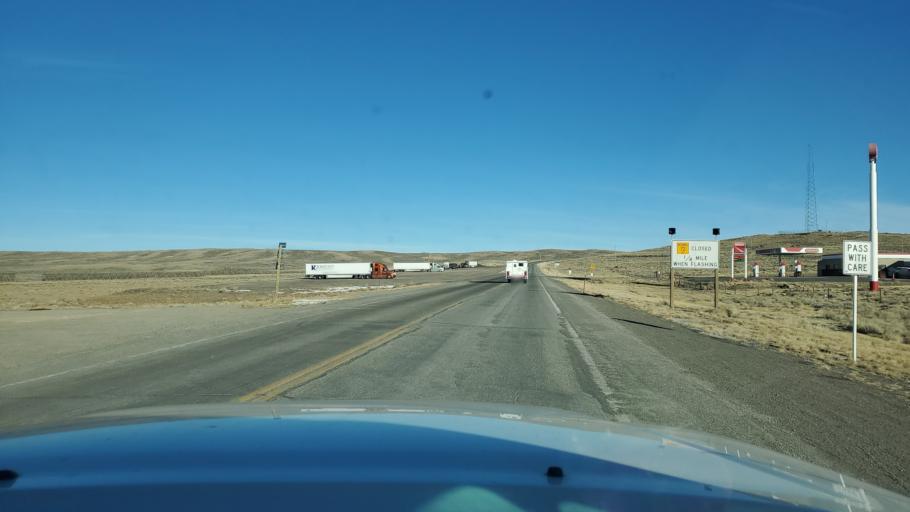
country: US
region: Wyoming
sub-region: Carbon County
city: Saratoga
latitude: 41.7259
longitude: -106.4598
